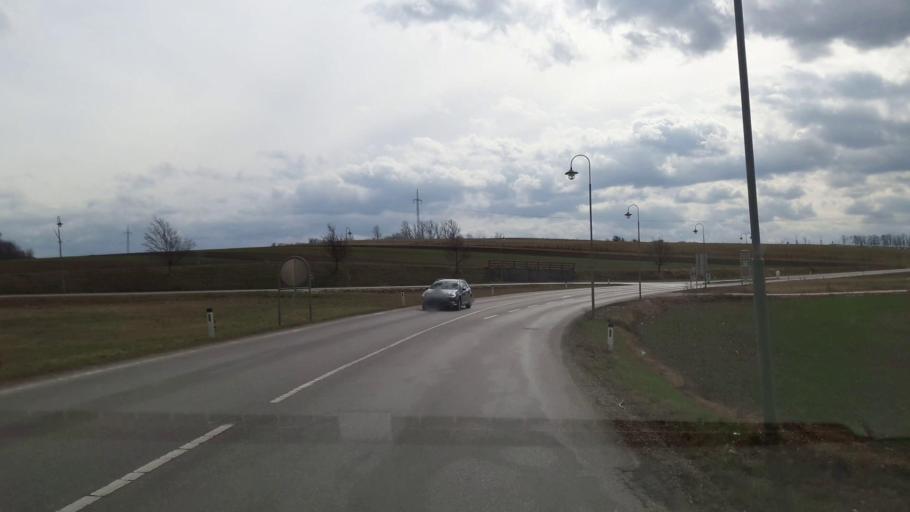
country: AT
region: Lower Austria
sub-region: Politischer Bezirk Mistelbach
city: Mistelbach
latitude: 48.5563
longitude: 16.5630
